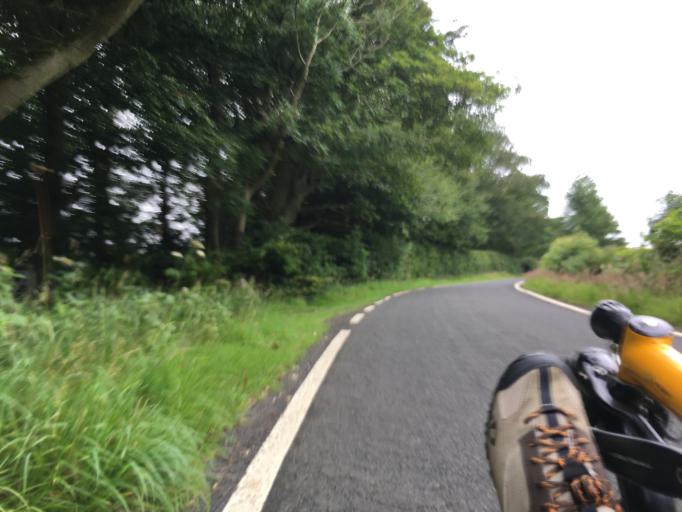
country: GB
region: Scotland
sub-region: West Lothian
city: West Calder
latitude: 55.8447
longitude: -3.5268
